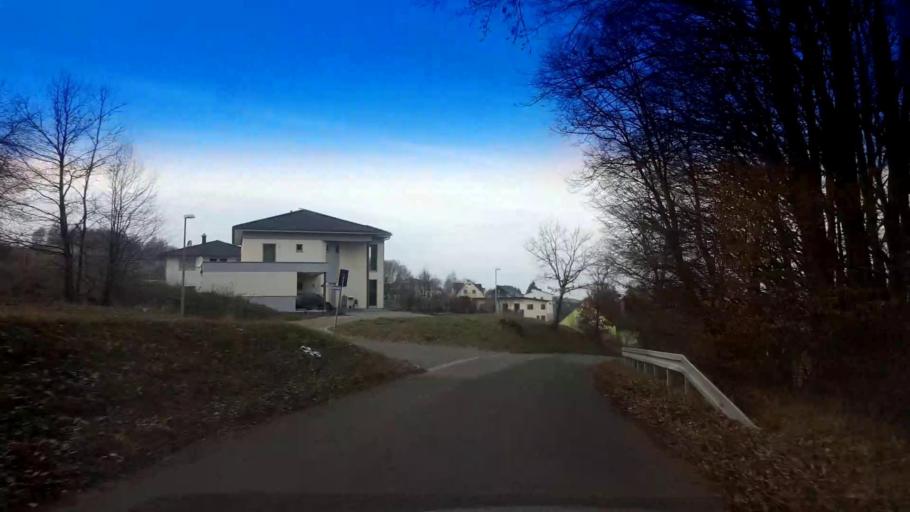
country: DE
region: Bavaria
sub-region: Upper Franconia
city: Hirschaid
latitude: 49.8024
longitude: 10.9887
